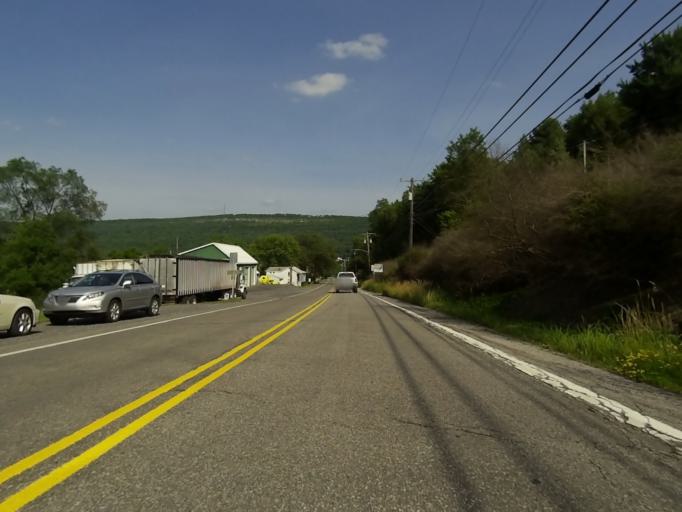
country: US
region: Pennsylvania
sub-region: Centre County
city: Stormstown
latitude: 40.8020
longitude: -78.0593
